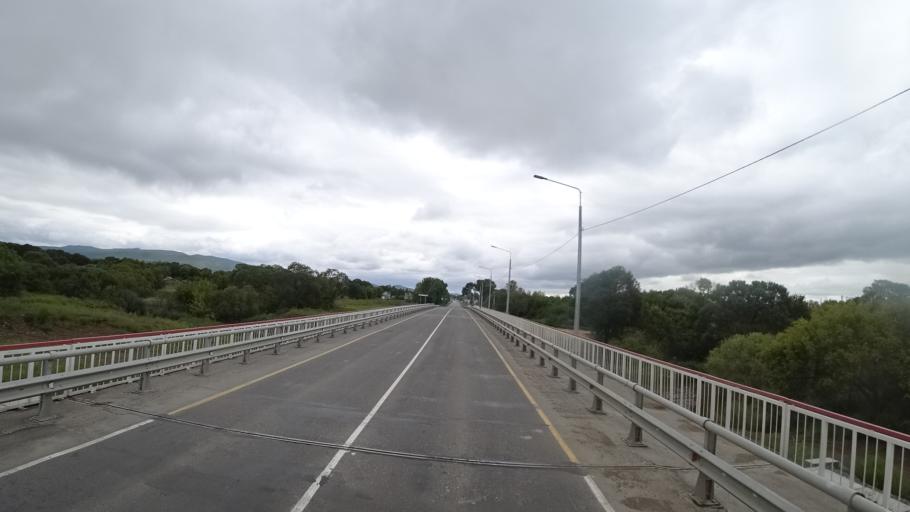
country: RU
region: Primorskiy
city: Chernigovka
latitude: 44.3428
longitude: 132.5910
